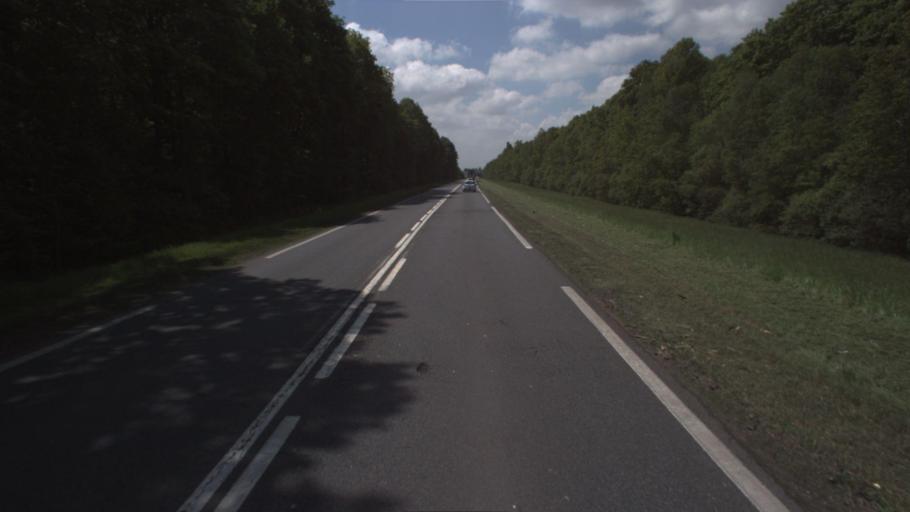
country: FR
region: Ile-de-France
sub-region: Departement de Seine-et-Marne
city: Guignes
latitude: 48.6477
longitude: 2.8008
